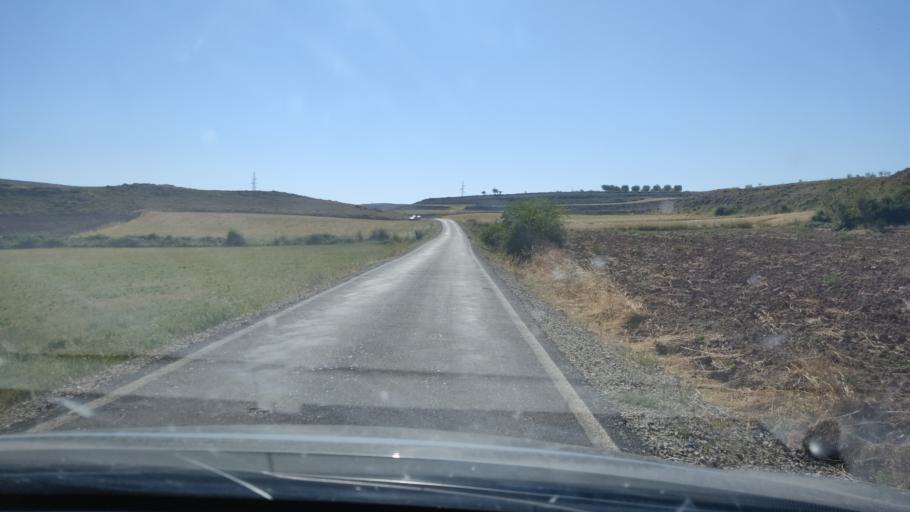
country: ES
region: Aragon
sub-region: Provincia de Teruel
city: Monforte de Moyuela
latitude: 41.0433
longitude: -0.9959
